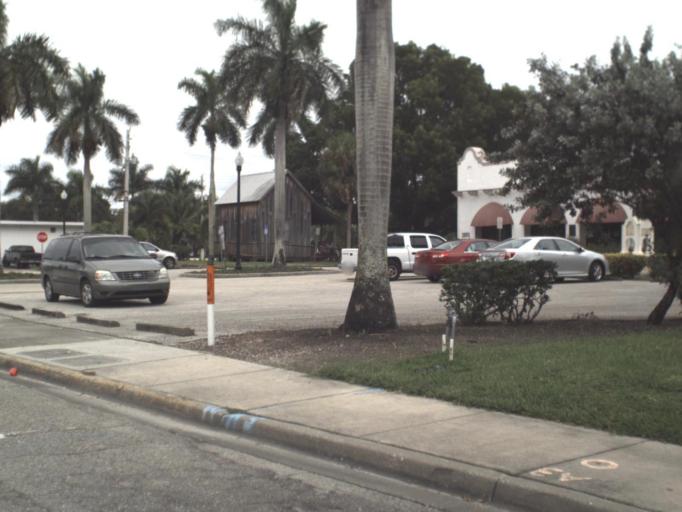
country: US
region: Florida
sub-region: Lee County
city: North Fort Myers
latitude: 26.6397
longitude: -81.8667
